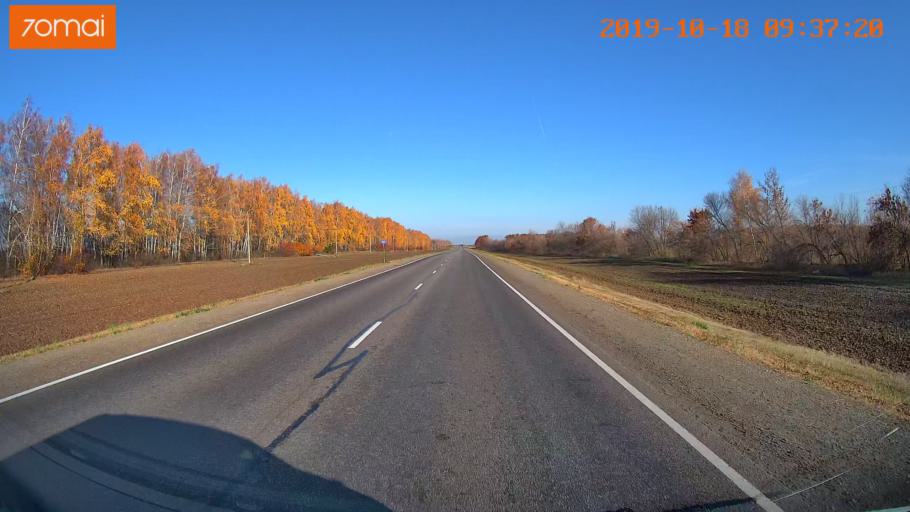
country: RU
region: Tula
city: Yefremov
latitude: 53.2205
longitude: 38.1415
